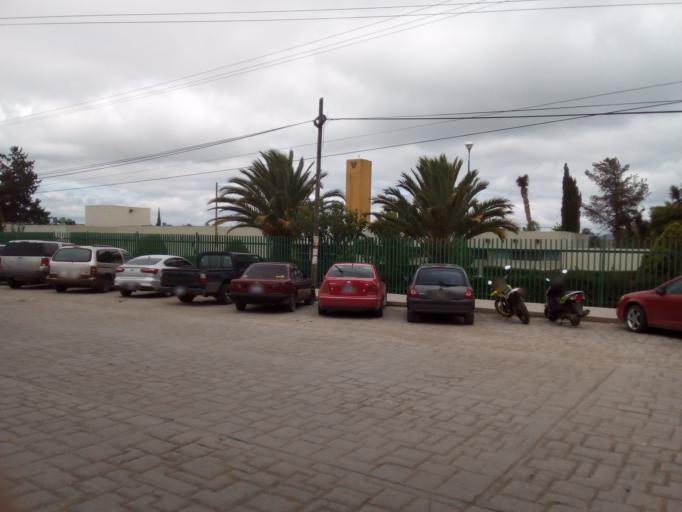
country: MX
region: Guerrero
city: San Luis de la Paz
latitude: 21.2956
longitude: -100.5298
